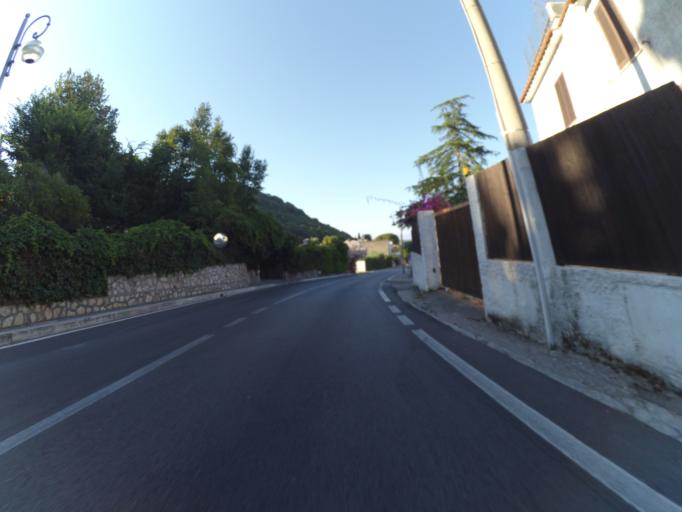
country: IT
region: Latium
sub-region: Provincia di Latina
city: San Felice Circeo
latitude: 41.2377
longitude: 13.0901
